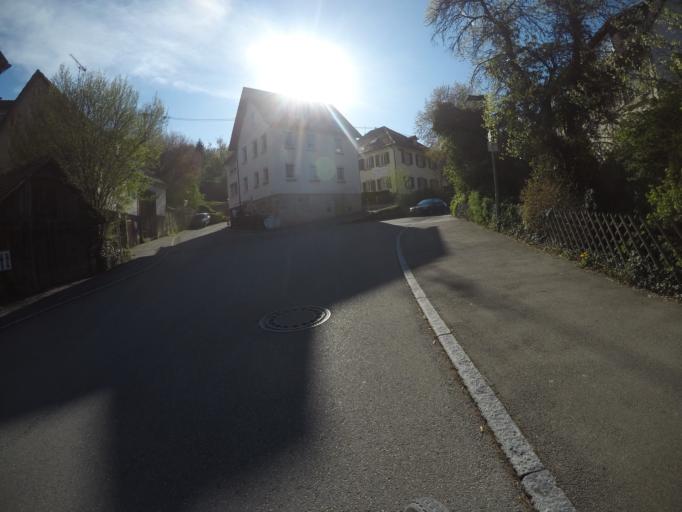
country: DE
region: Baden-Wuerttemberg
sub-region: Regierungsbezirk Stuttgart
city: Schlaitdorf
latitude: 48.6225
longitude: 9.2048
